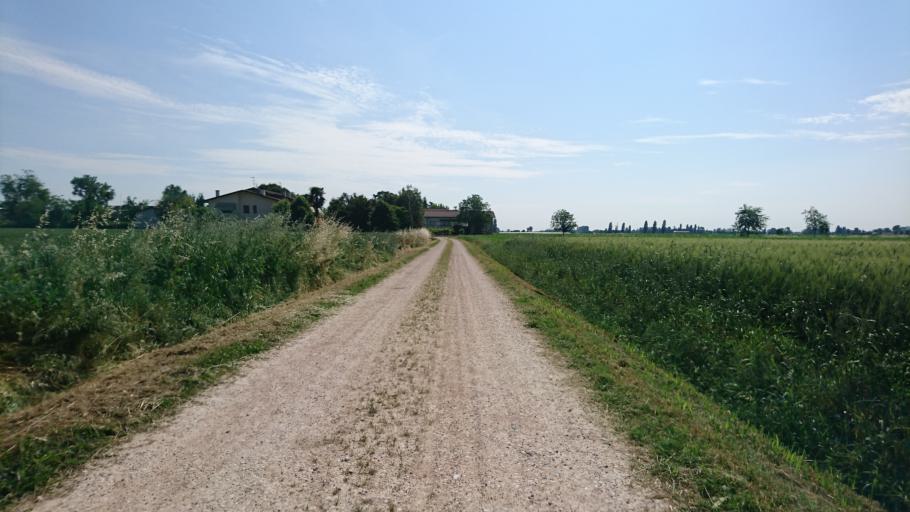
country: IT
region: Veneto
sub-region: Provincia di Padova
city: Casale di Scodosia
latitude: 45.1828
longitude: 11.4920
